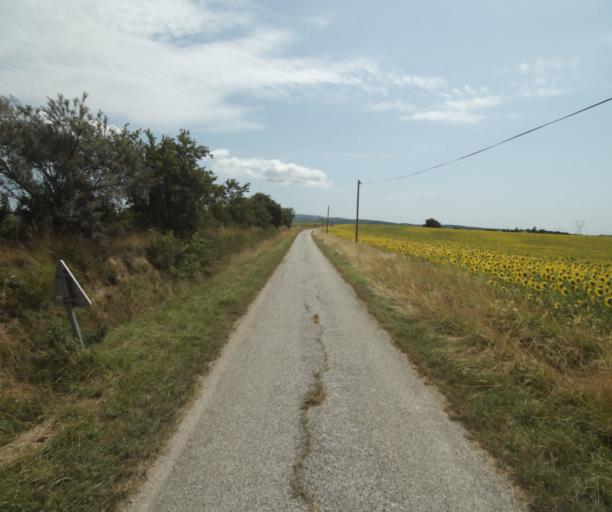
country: FR
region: Midi-Pyrenees
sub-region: Departement de la Haute-Garonne
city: Saint-Felix-Lauragais
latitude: 43.4161
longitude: 1.9082
